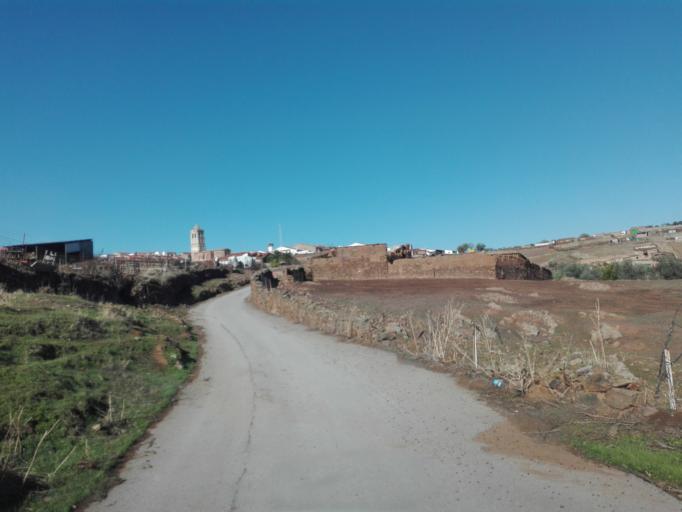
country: ES
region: Extremadura
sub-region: Provincia de Badajoz
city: Llera
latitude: 38.4466
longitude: -6.0514
